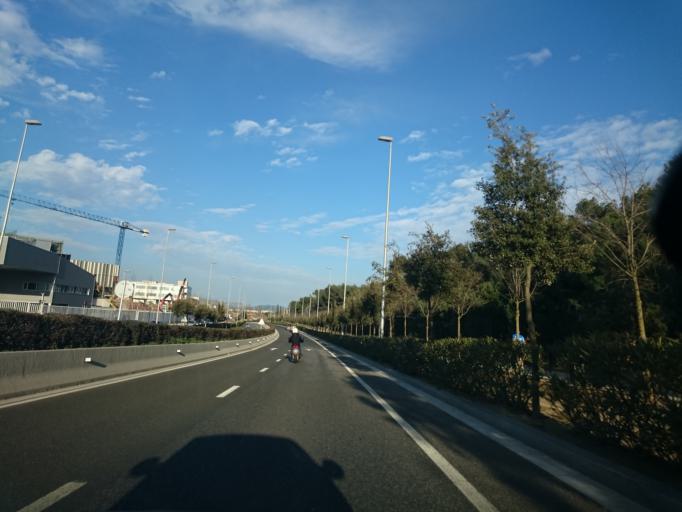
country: ES
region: Catalonia
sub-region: Provincia de Barcelona
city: Sant Cugat del Valles
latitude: 41.4827
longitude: 2.1069
